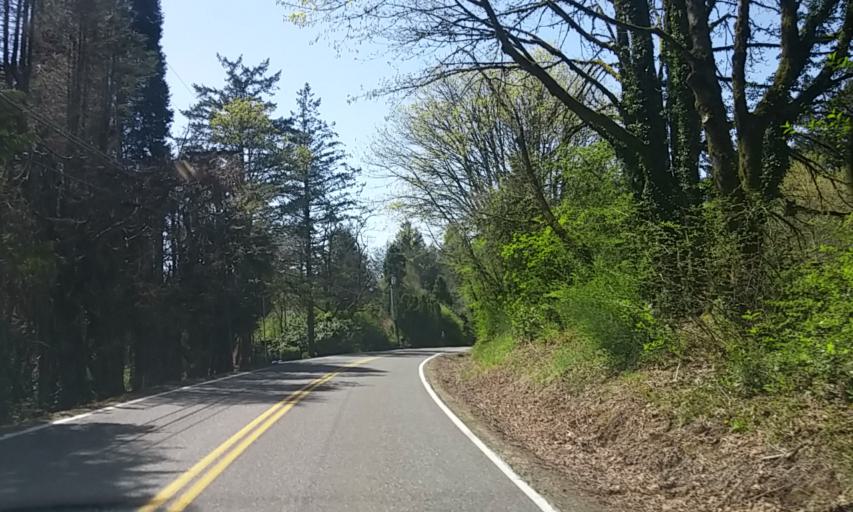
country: US
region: Oregon
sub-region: Washington County
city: West Haven-Sylvan
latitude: 45.5248
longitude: -122.7502
